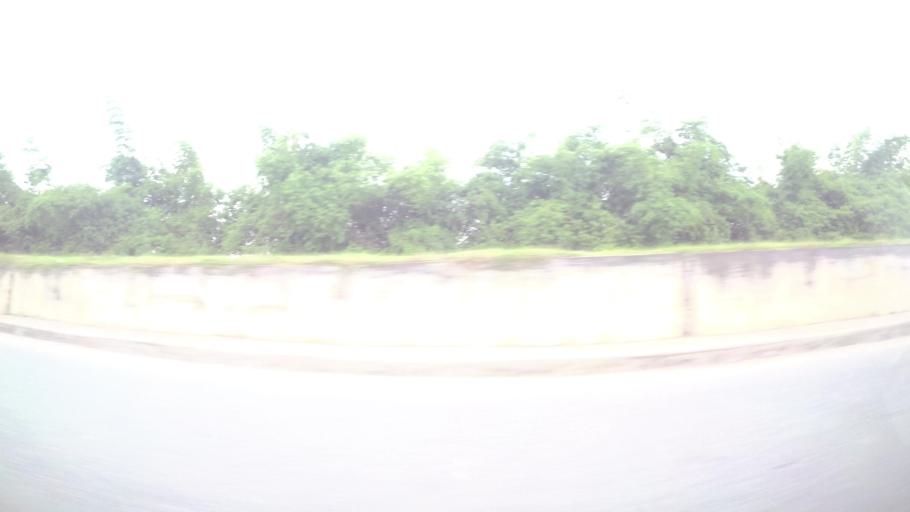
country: VN
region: Ha Noi
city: Trau Quy
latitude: 21.0438
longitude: 105.9308
